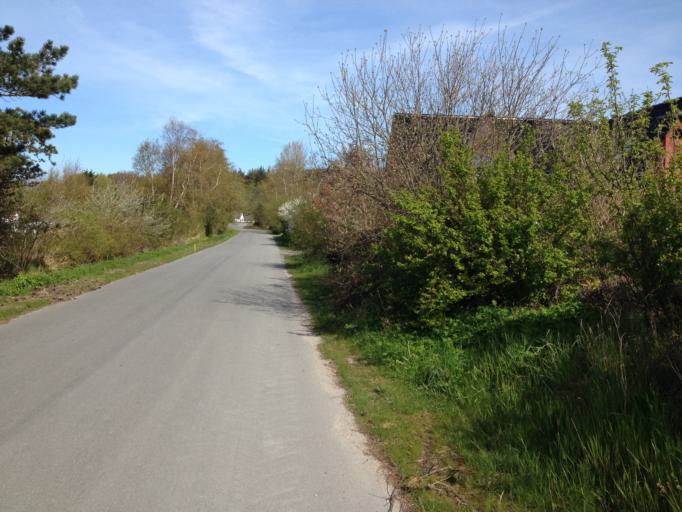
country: DK
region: Capital Region
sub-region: Halsnaes Kommune
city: Hundested
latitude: 55.9454
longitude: 11.9019
